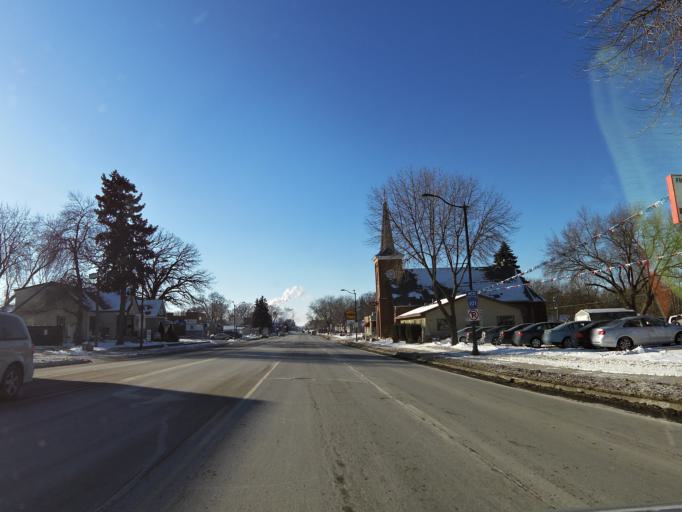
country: US
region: Minnesota
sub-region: Scott County
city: Shakopee
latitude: 44.7998
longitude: -93.5169
